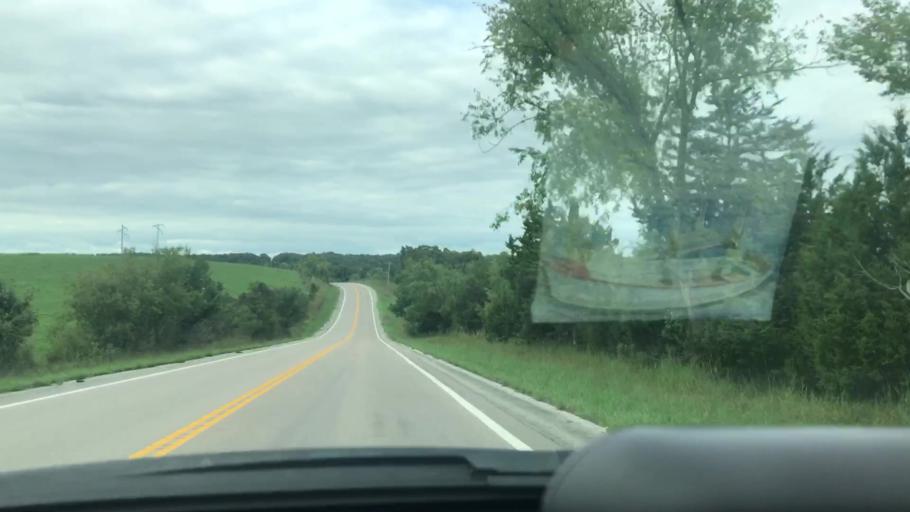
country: US
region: Missouri
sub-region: Benton County
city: Warsaw
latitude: 38.1283
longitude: -93.2804
